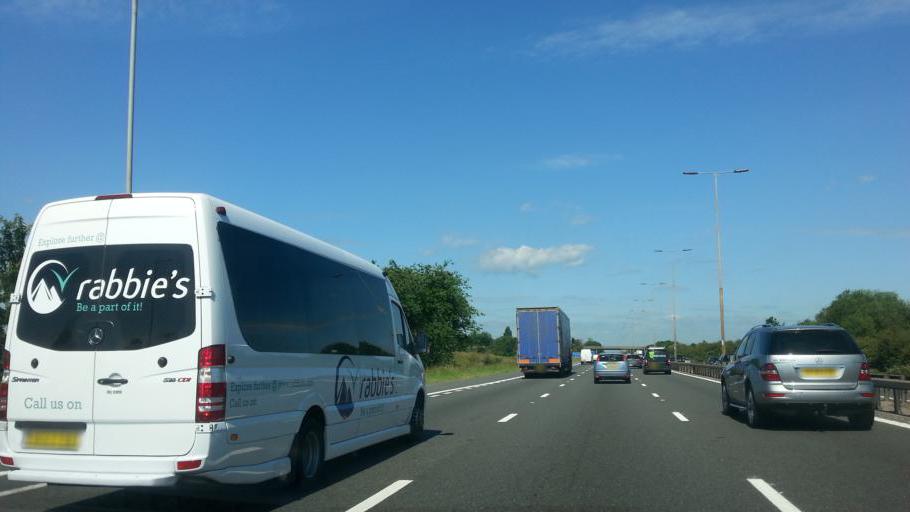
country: GB
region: England
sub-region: West Berkshire
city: Eton
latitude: 51.5052
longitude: -0.6264
